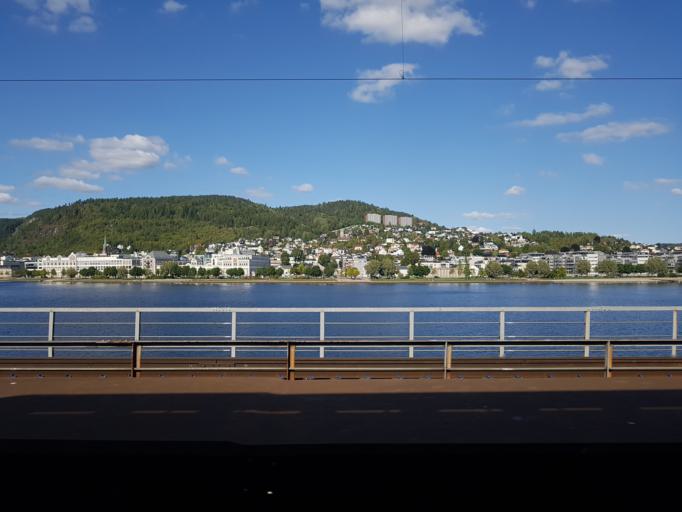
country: NO
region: Buskerud
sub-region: Drammen
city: Drammen
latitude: 59.7370
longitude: 10.2132
